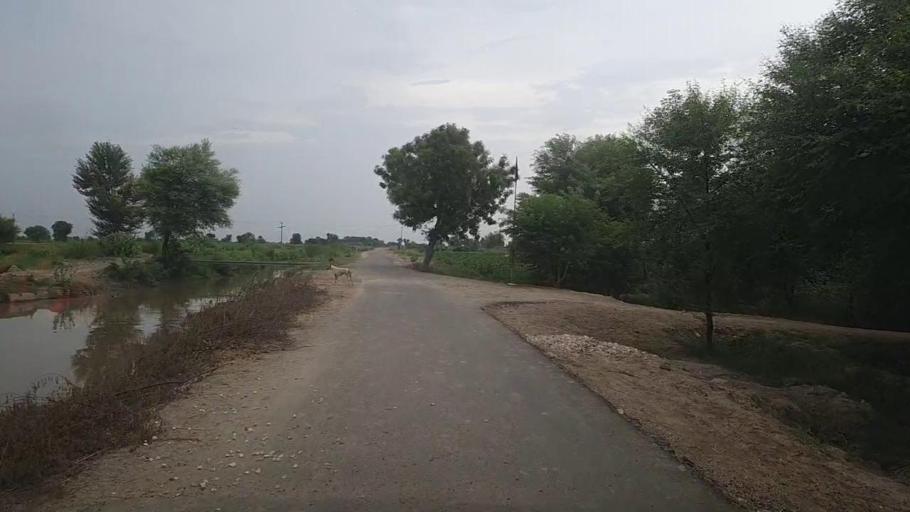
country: PK
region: Sindh
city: Karaundi
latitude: 26.9683
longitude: 68.3629
